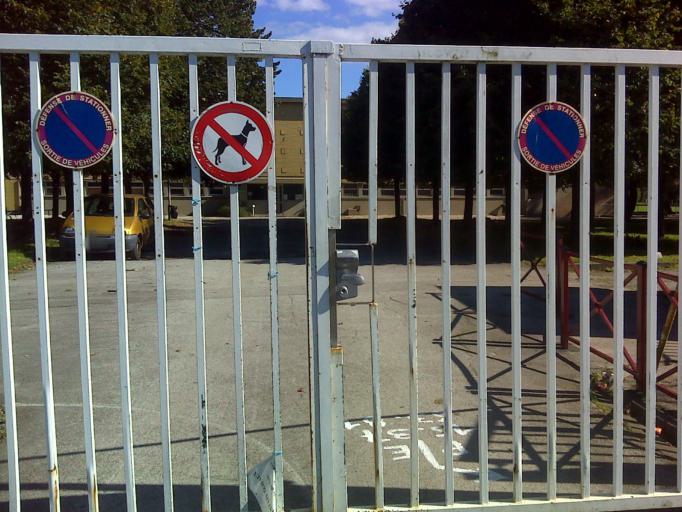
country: FR
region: Nord-Pas-de-Calais
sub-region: Departement du Nord
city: Coudekerque-Branche
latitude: 51.0122
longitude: 2.3805
